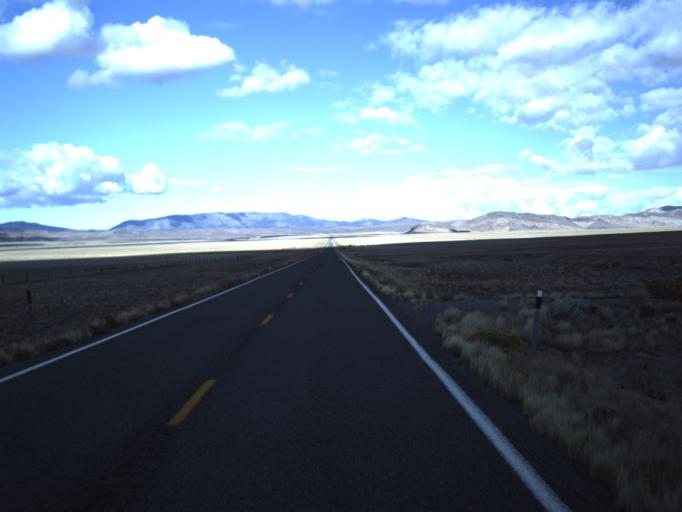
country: US
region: Utah
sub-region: Beaver County
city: Milford
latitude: 38.5515
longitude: -113.7337
